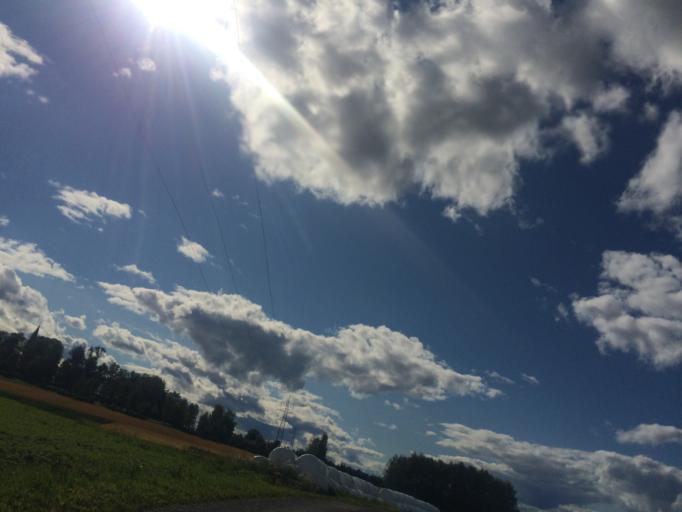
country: NO
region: Akershus
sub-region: As
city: As
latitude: 59.6733
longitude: 10.7749
